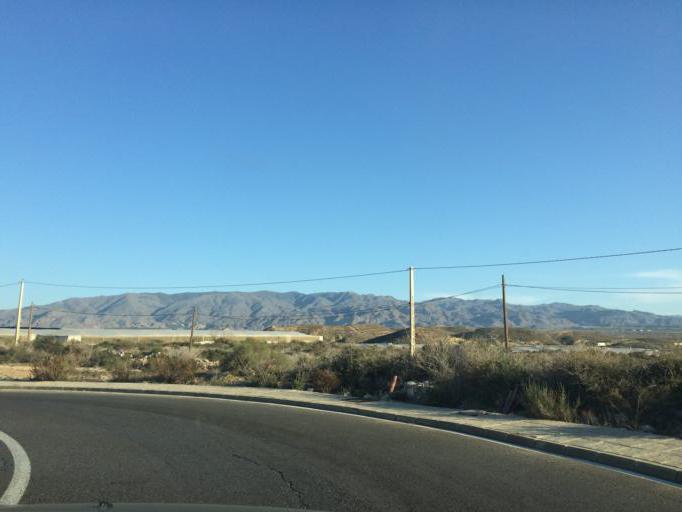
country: ES
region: Andalusia
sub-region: Provincia de Almeria
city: Viator
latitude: 36.8789
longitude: -2.4111
